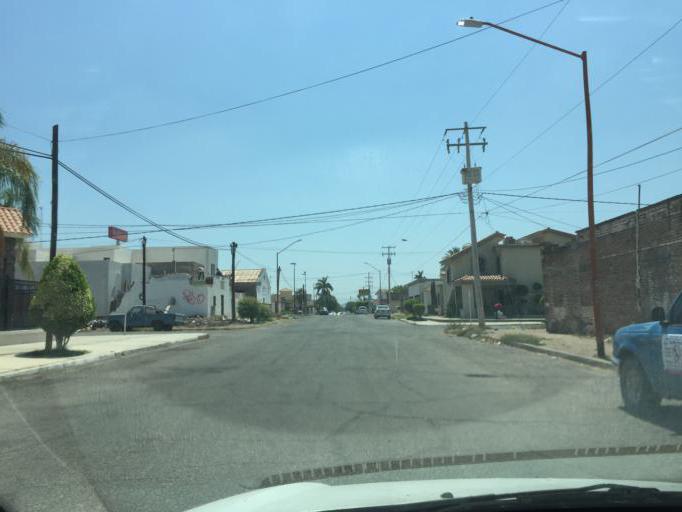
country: MX
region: Sonora
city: Navojoa
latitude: 27.0781
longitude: -109.4549
